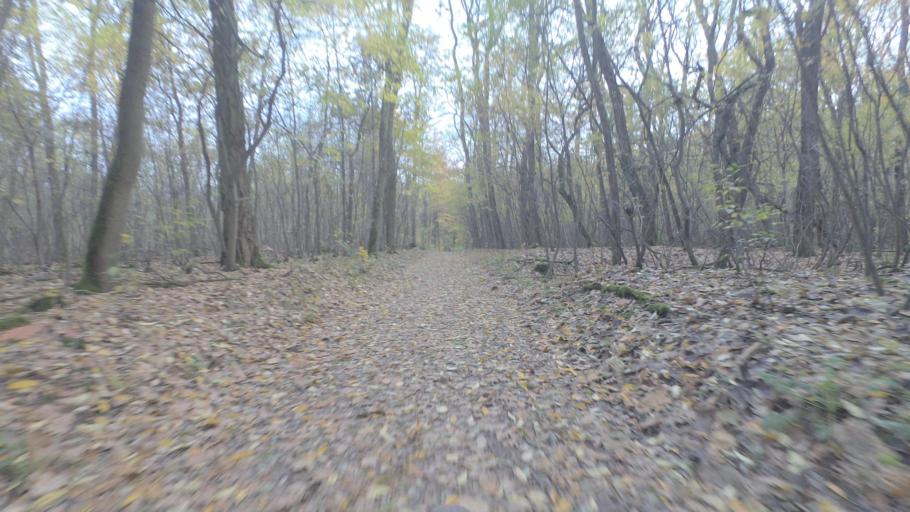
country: DE
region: Brandenburg
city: Rangsdorf
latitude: 52.3123
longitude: 13.4191
